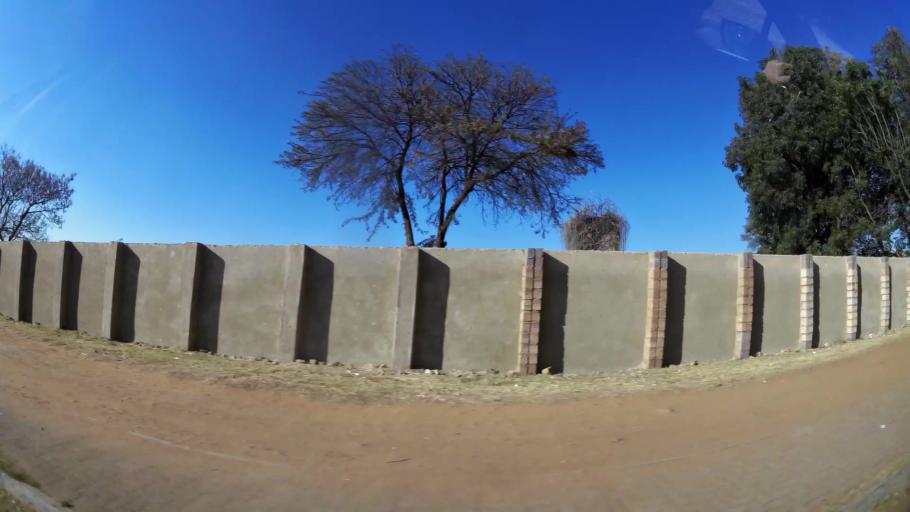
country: ZA
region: Gauteng
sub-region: City of Johannesburg Metropolitan Municipality
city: Roodepoort
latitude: -26.1522
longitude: 27.8354
